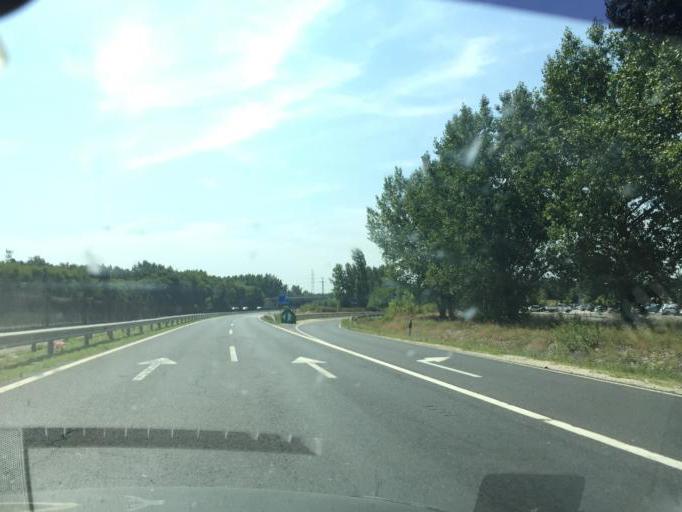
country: HU
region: Pest
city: Fot
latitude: 47.6216
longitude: 19.1683
